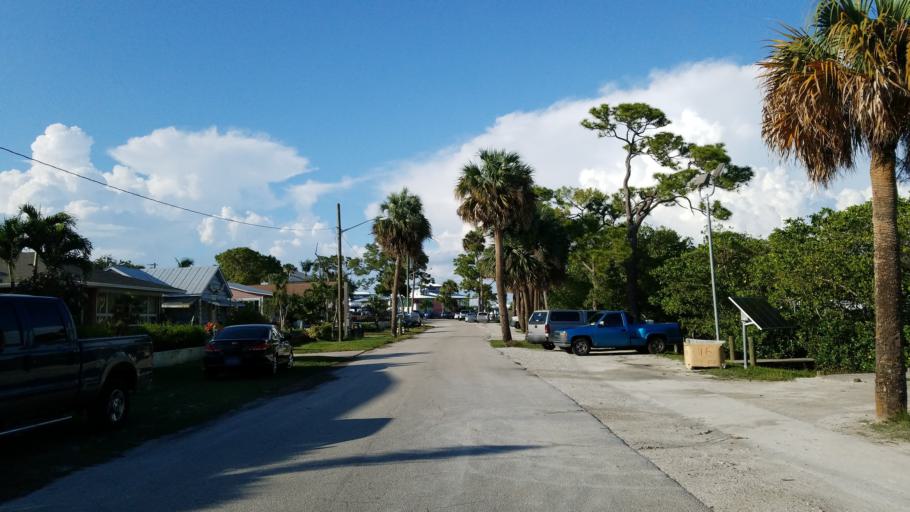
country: US
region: Florida
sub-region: Martin County
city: Port Salerno
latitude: 27.1481
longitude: -80.1960
